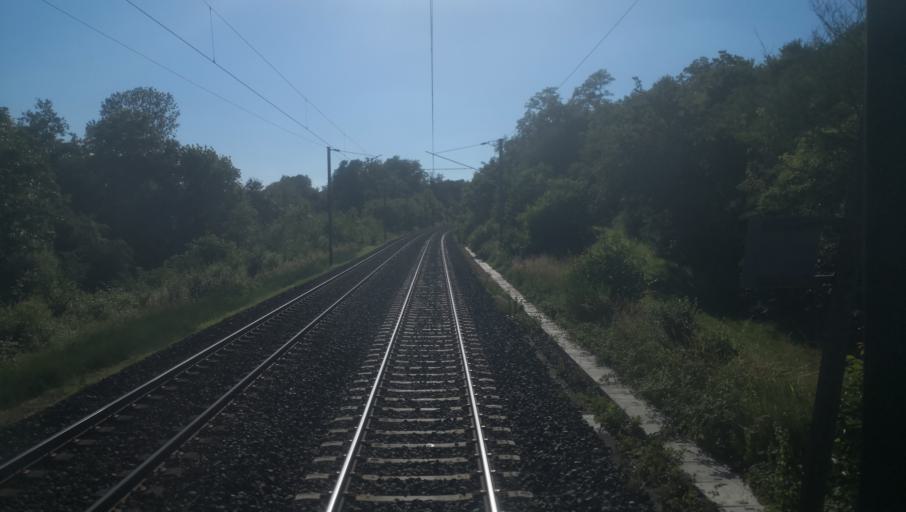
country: FR
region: Centre
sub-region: Departement du Cher
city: Saint-Satur
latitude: 47.3176
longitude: 2.8951
